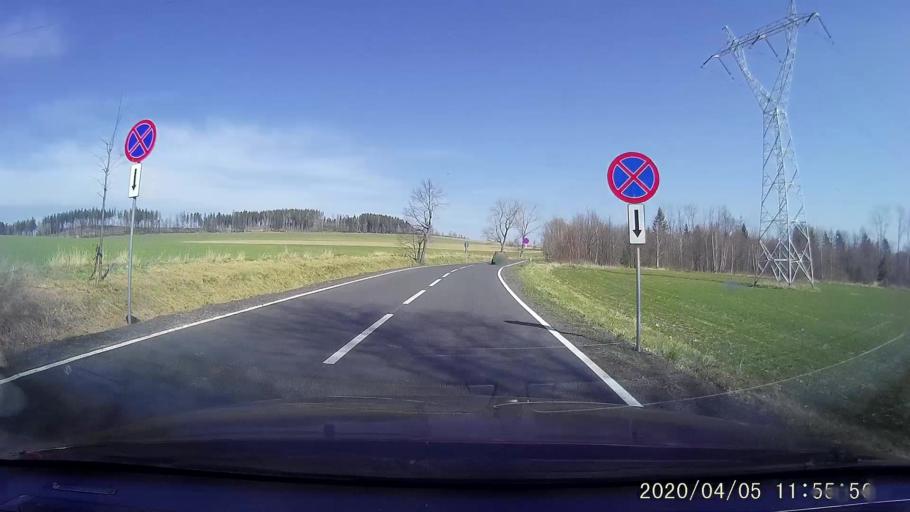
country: PL
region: Lower Silesian Voivodeship
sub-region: Powiat lubanski
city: Lesna
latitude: 50.9797
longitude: 15.3102
